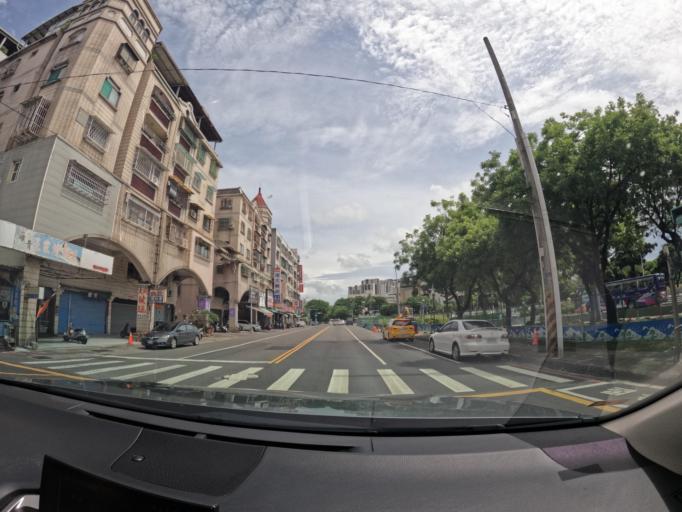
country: TW
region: Kaohsiung
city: Kaohsiung
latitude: 22.6763
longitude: 120.2868
